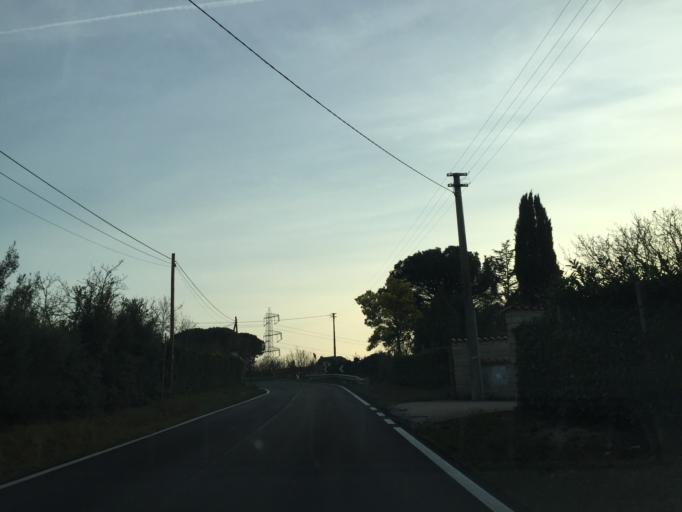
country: IT
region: Latium
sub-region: Citta metropolitana di Roma Capitale
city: Mazzano Romano
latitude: 42.1813
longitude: 12.3632
